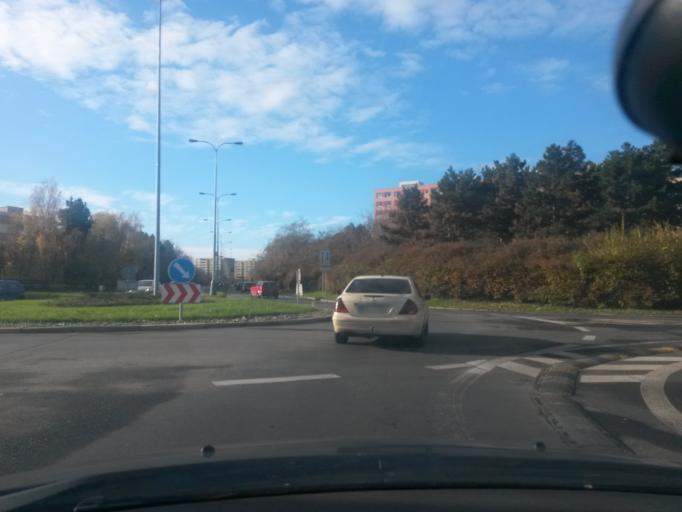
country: CZ
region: Central Bohemia
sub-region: Okres Praha-Zapad
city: Pruhonice
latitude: 50.0294
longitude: 14.5258
